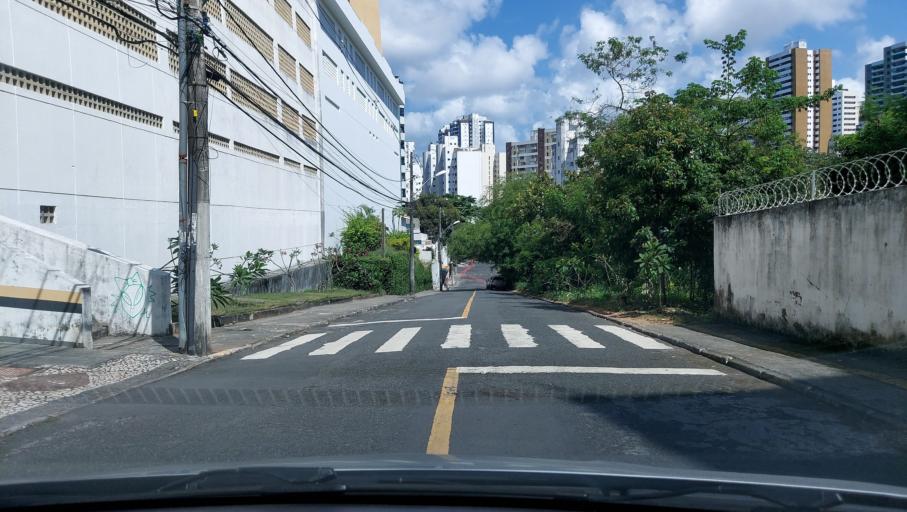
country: BR
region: Bahia
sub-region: Salvador
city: Salvador
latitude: -12.9866
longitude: -38.4594
